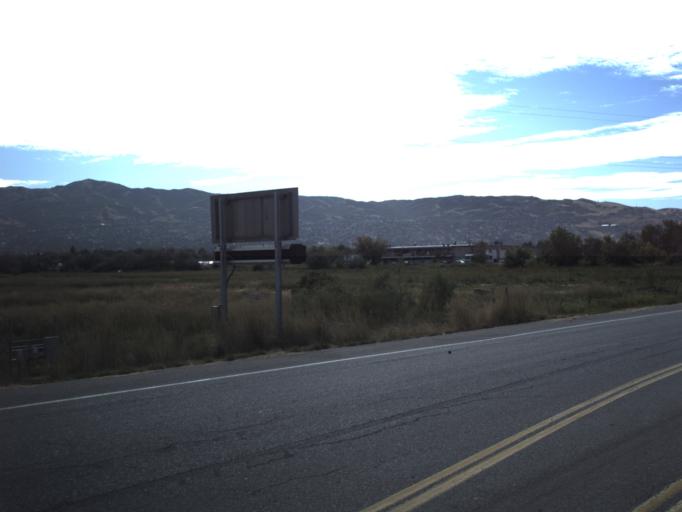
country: US
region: Utah
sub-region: Davis County
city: West Bountiful
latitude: 40.8830
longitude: -111.9300
